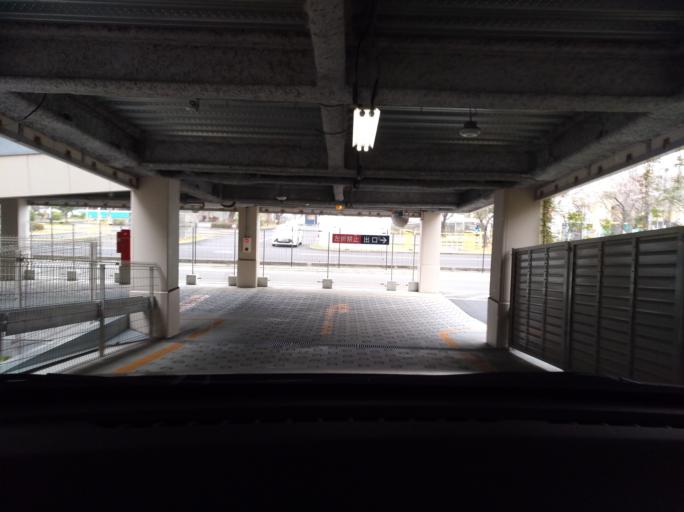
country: JP
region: Tokyo
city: Chofugaoka
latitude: 35.6581
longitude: 139.5672
